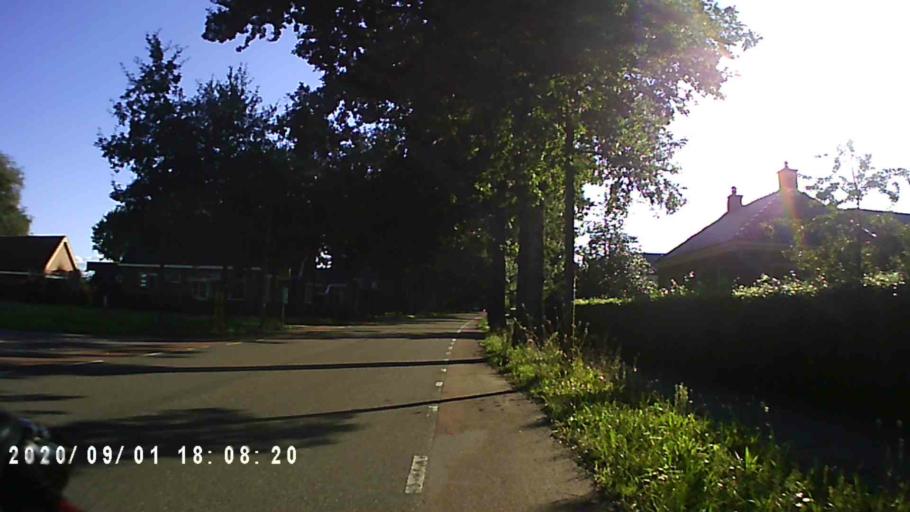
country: NL
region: Groningen
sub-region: Gemeente Slochteren
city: Slochteren
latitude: 53.1974
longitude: 6.7859
